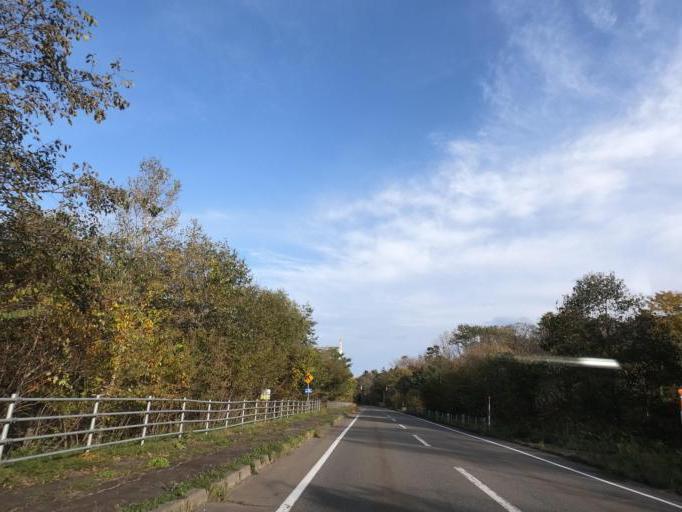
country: JP
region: Hokkaido
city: Obihiro
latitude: 42.5009
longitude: 143.4072
